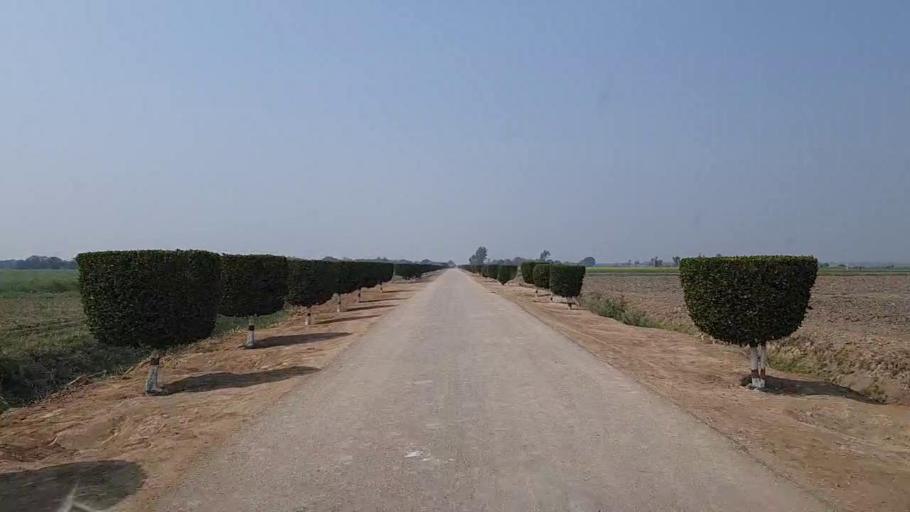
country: PK
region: Sindh
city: Mirwah Gorchani
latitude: 25.3357
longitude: 69.0021
